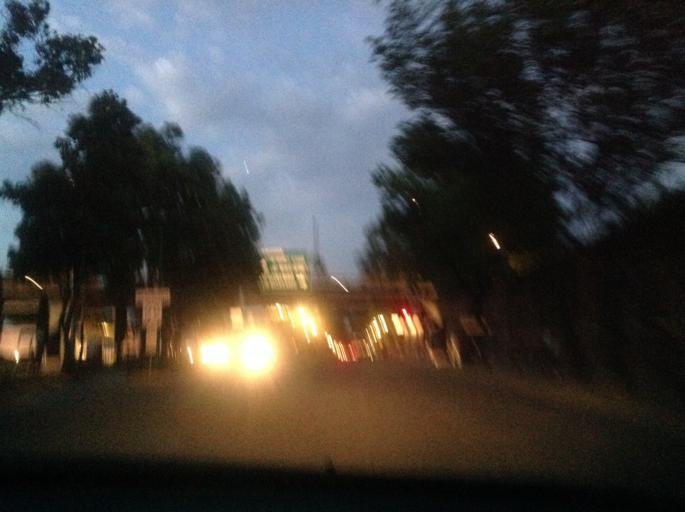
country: MX
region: Mexico City
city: Miguel Hidalgo
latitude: 19.4474
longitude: -99.2065
